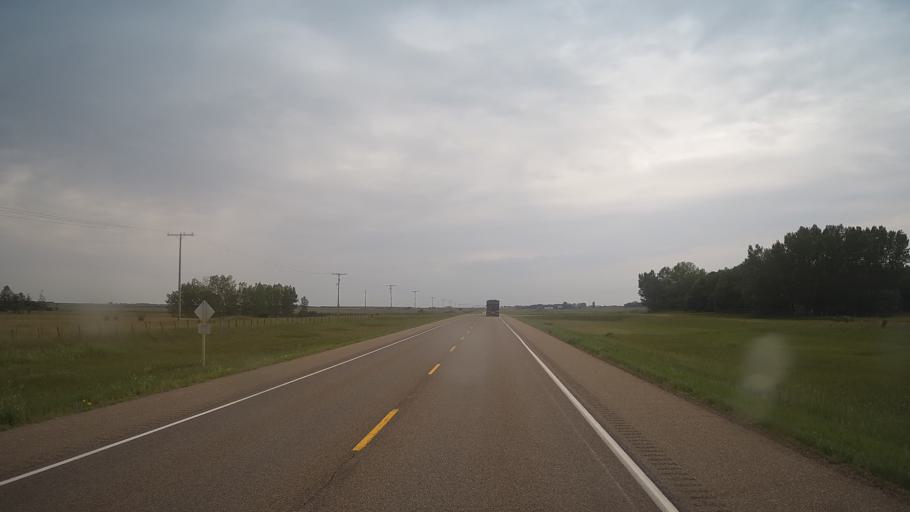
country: CA
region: Saskatchewan
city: Langham
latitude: 52.1289
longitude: -107.1417
